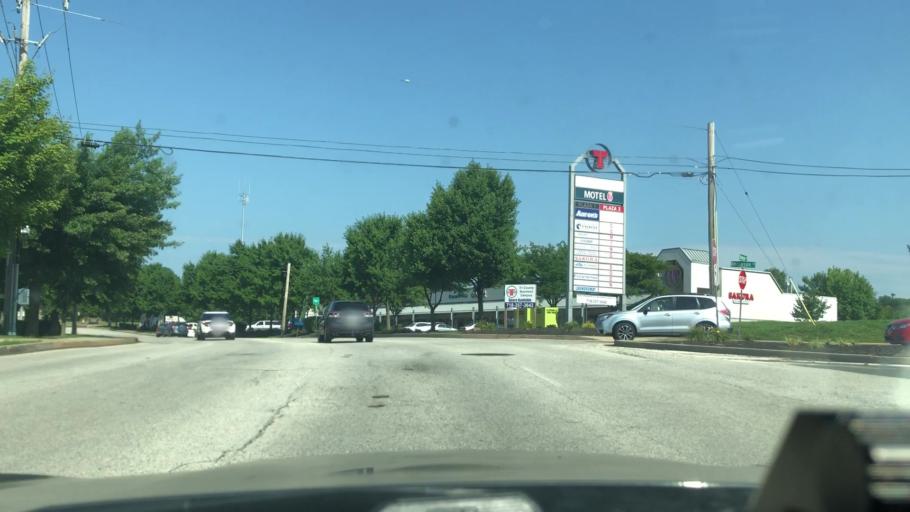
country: US
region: Pennsylvania
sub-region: Montgomery County
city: Pottstown
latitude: 40.2548
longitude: -75.6603
